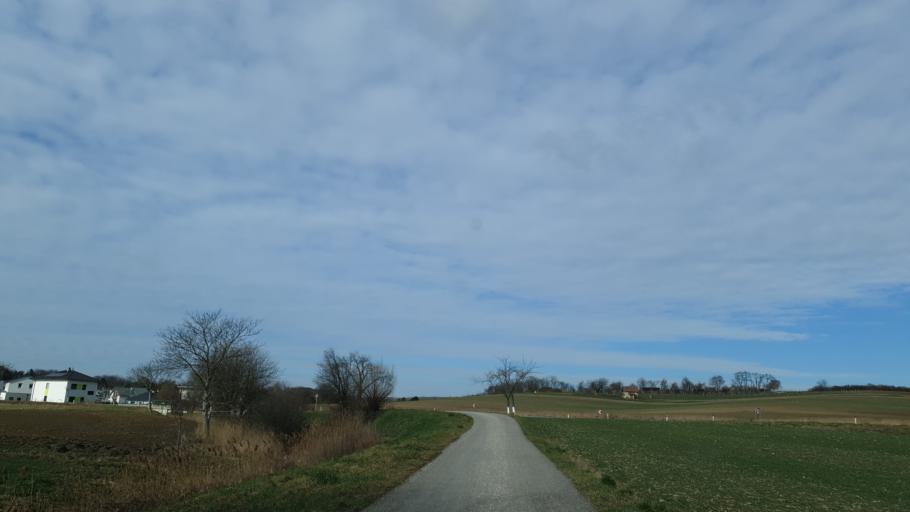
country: AT
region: Lower Austria
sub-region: Politischer Bezirk Mistelbach
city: Grossebersdorf
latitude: 48.3843
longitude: 16.4832
